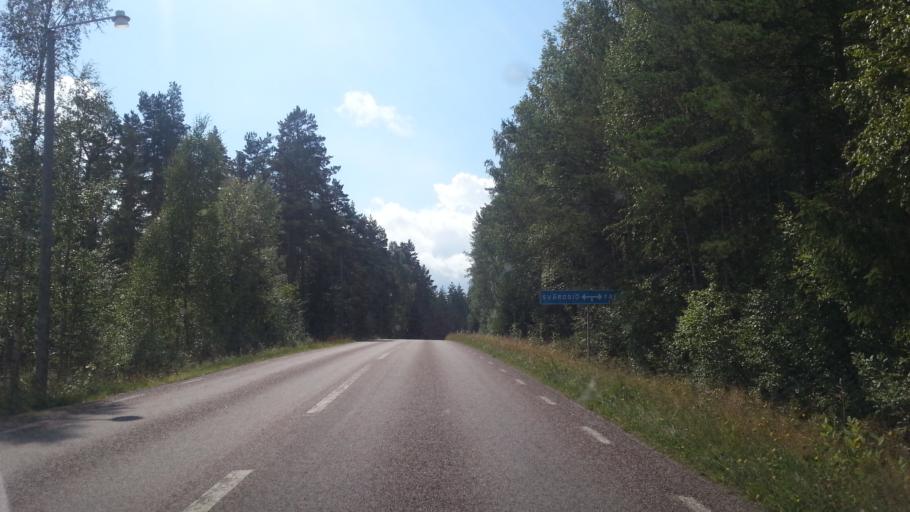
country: SE
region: Dalarna
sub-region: Faluns Kommun
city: Falun
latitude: 60.6191
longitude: 15.7660
